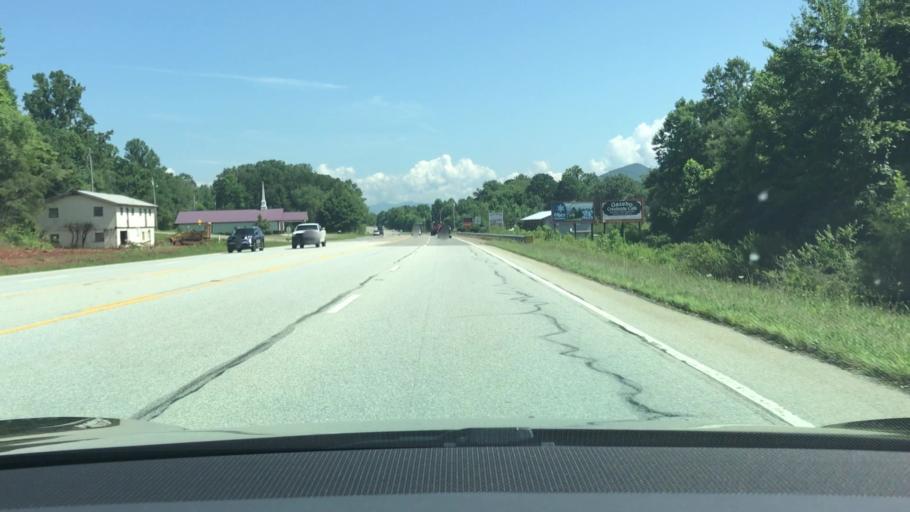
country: US
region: North Carolina
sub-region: Macon County
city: Franklin
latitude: 35.0709
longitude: -83.3871
